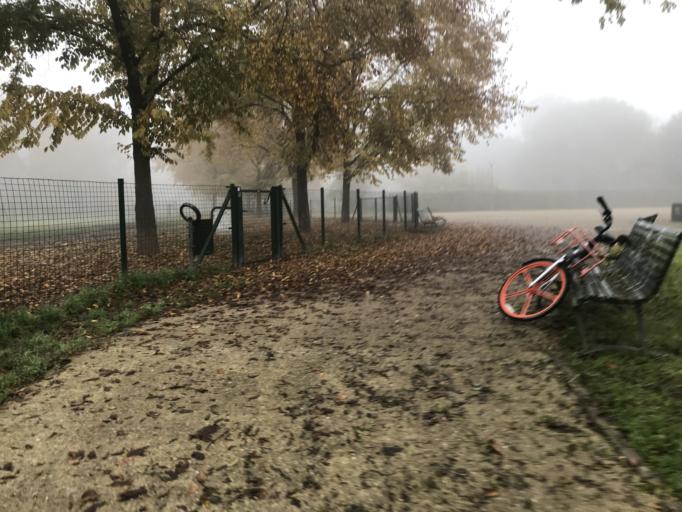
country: IT
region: Lombardy
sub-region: Citta metropolitana di Milano
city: Novegro-Tregarezzo-San Felice
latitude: 45.4787
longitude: 9.2520
